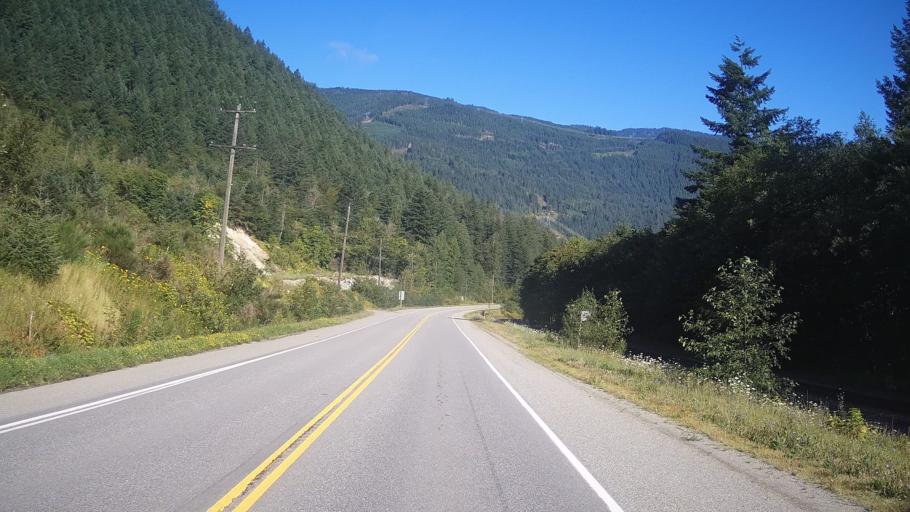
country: CA
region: British Columbia
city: Hope
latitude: 49.5387
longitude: -121.4329
